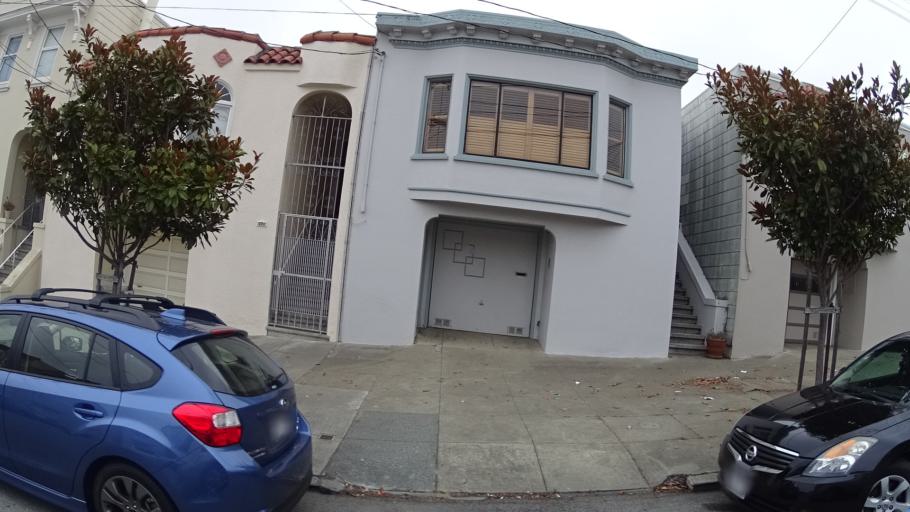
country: US
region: California
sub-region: San Francisco County
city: San Francisco
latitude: 37.7752
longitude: -122.4876
